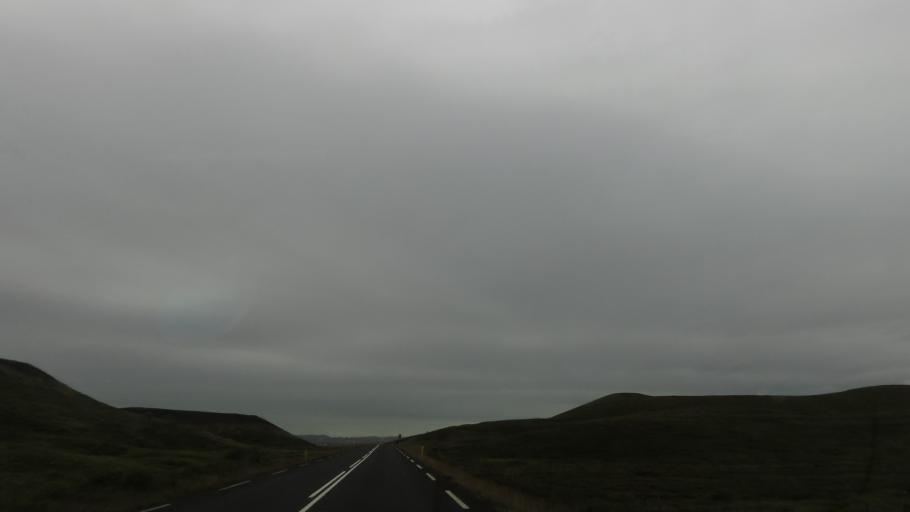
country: IS
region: Northeast
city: Laugar
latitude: 65.6173
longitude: -17.0353
